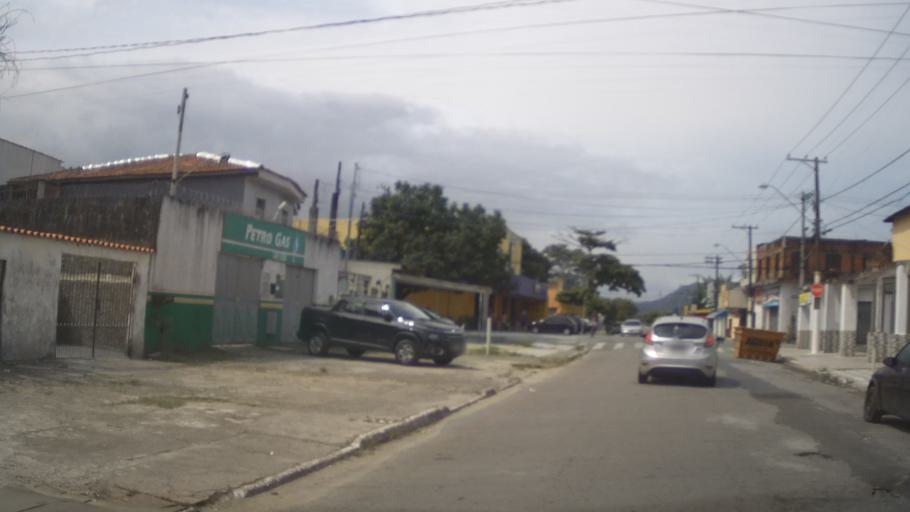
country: BR
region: Sao Paulo
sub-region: Praia Grande
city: Praia Grande
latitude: -24.0116
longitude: -46.4511
